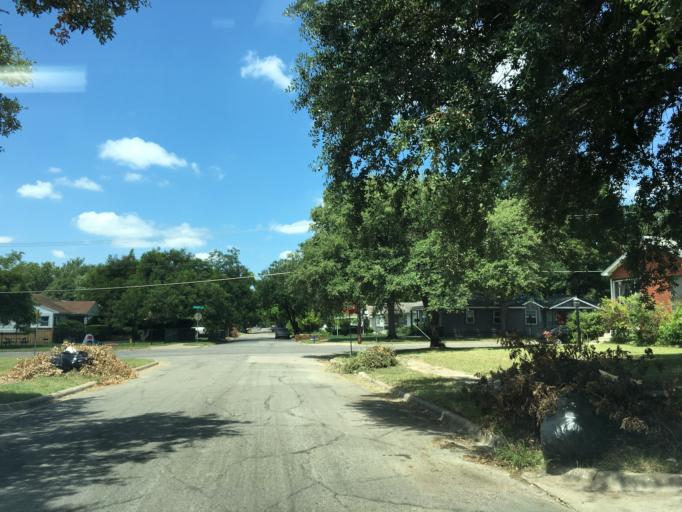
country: US
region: Texas
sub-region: Dallas County
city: Garland
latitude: 32.8393
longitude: -96.6727
